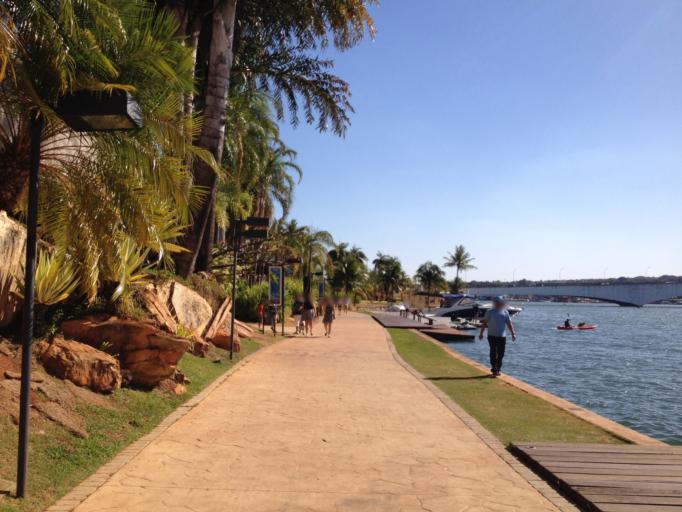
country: BR
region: Federal District
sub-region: Brasilia
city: Brasilia
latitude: -15.8246
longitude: -47.8739
